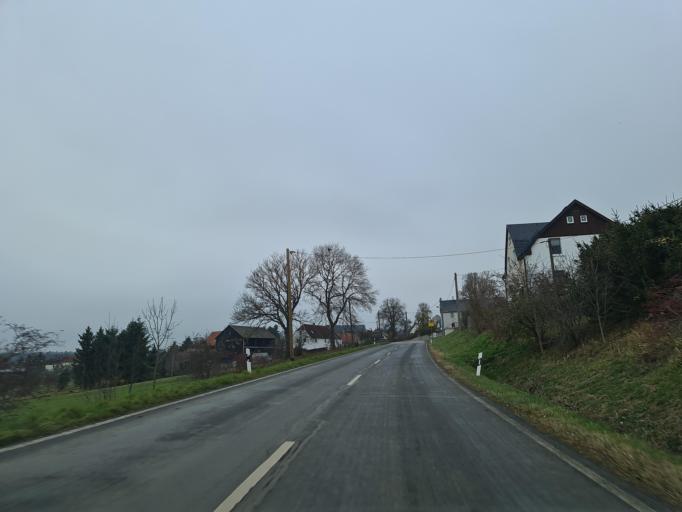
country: DE
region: Saxony
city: Mehltheuer
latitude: 50.5094
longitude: 12.0541
